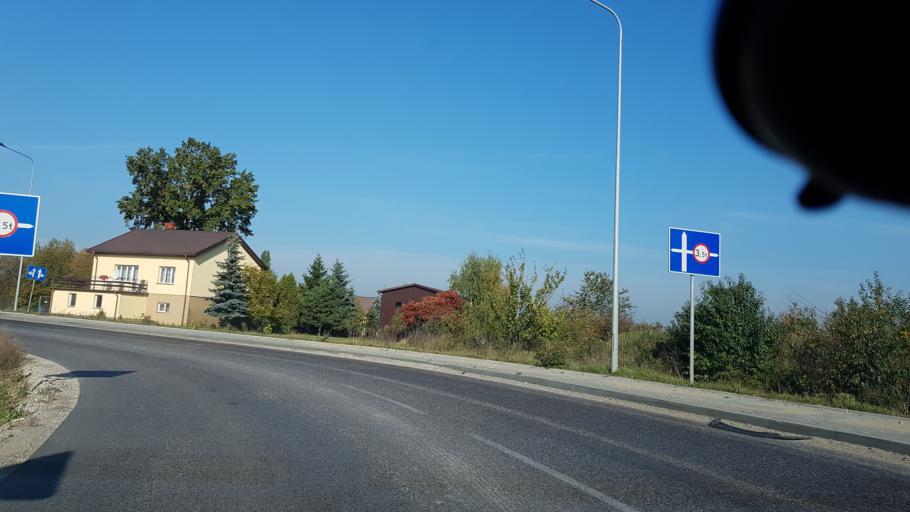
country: PL
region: Masovian Voivodeship
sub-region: Powiat pruszkowski
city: Nadarzyn
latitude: 52.0768
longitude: 20.7730
